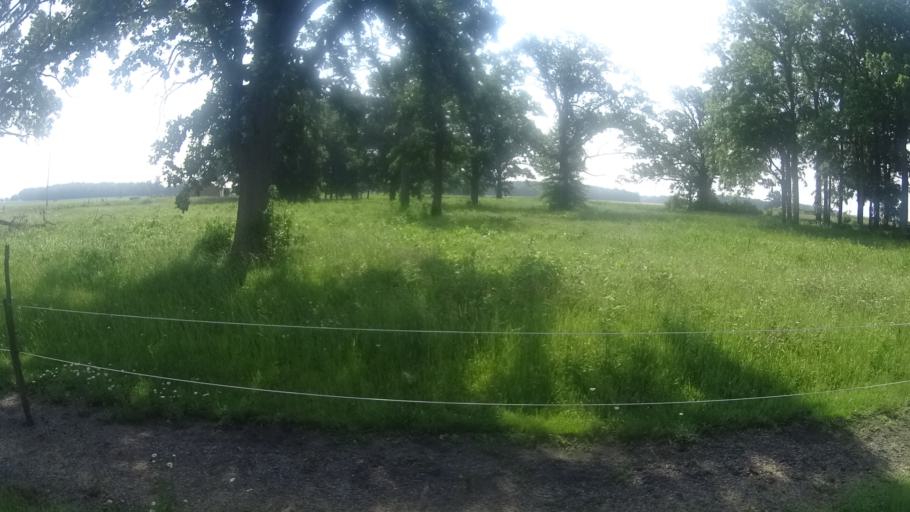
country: US
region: Ohio
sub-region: Huron County
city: Monroeville
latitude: 41.2884
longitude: -82.7462
